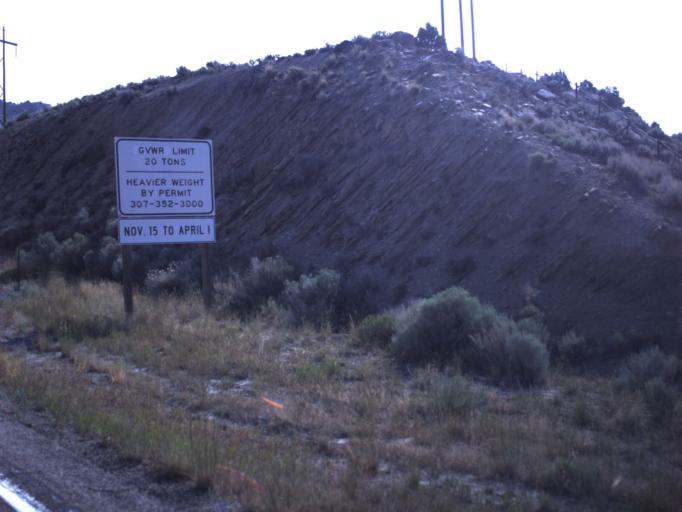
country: US
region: Utah
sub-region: Daggett County
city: Manila
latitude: 40.9999
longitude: -109.4307
